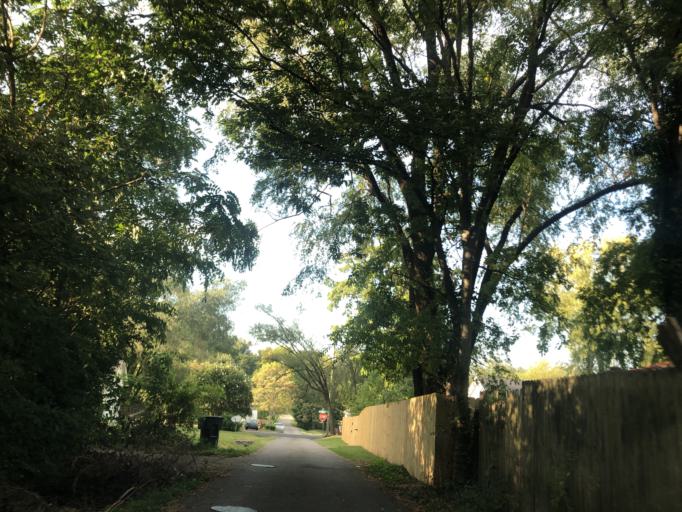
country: US
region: Tennessee
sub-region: Davidson County
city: Oak Hill
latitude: 36.1194
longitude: -86.7408
